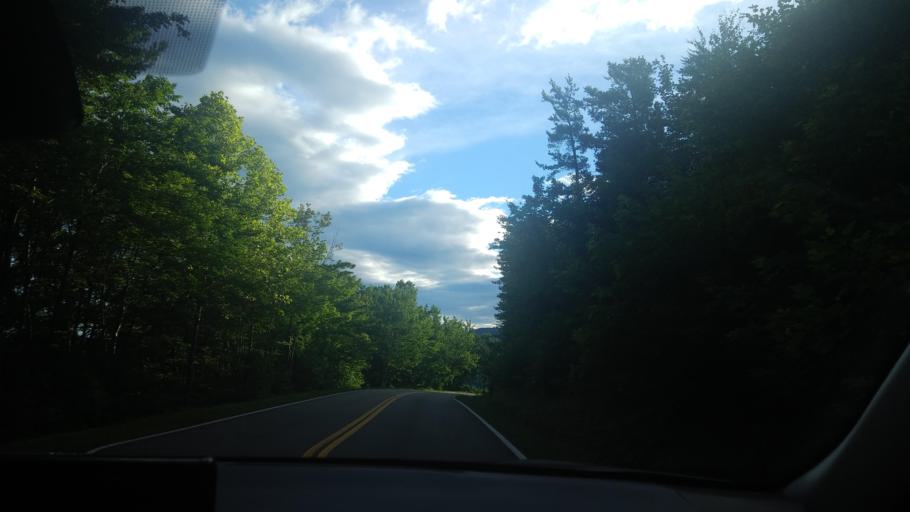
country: US
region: Tennessee
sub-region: Cocke County
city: Newport
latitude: 35.8238
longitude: -83.2125
